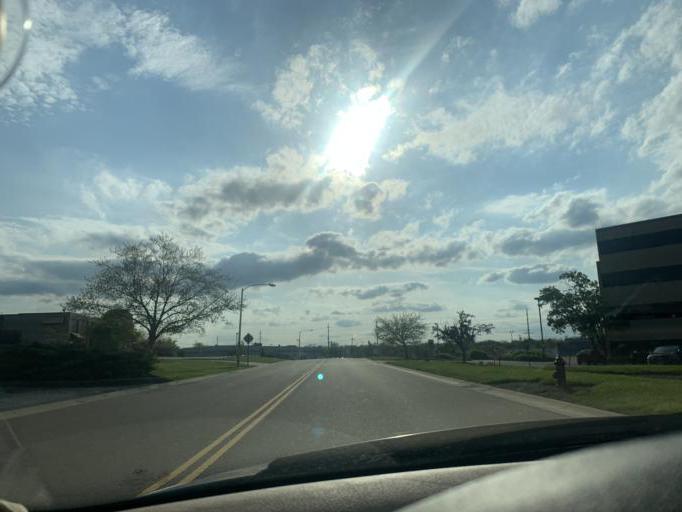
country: US
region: Ohio
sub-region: Hamilton County
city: Springdale
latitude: 39.2845
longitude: -84.4718
